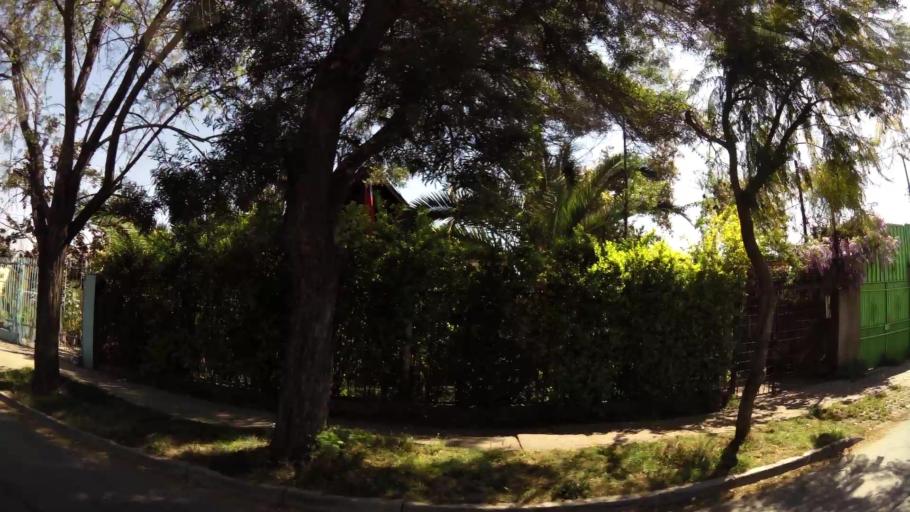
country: CL
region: Santiago Metropolitan
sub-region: Provincia de Santiago
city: La Pintana
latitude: -33.5305
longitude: -70.6378
